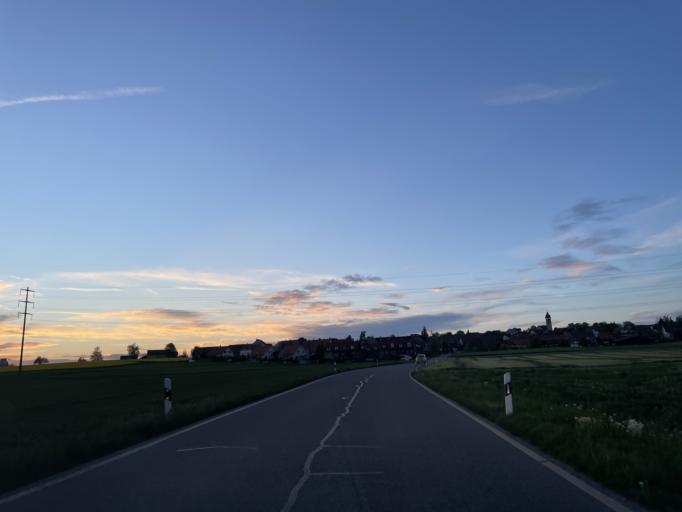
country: CH
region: Zurich
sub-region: Bezirk Winterthur
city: Brutten
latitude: 47.4672
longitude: 8.6756
